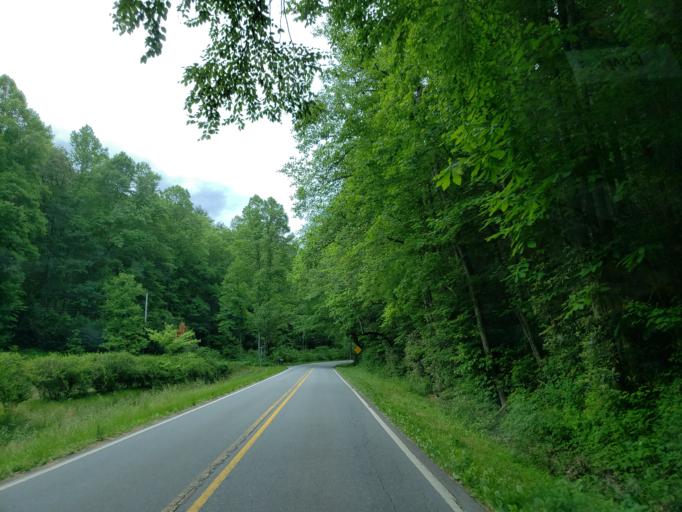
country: US
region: Georgia
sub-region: Fannin County
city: Blue Ridge
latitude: 34.8444
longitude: -84.3940
